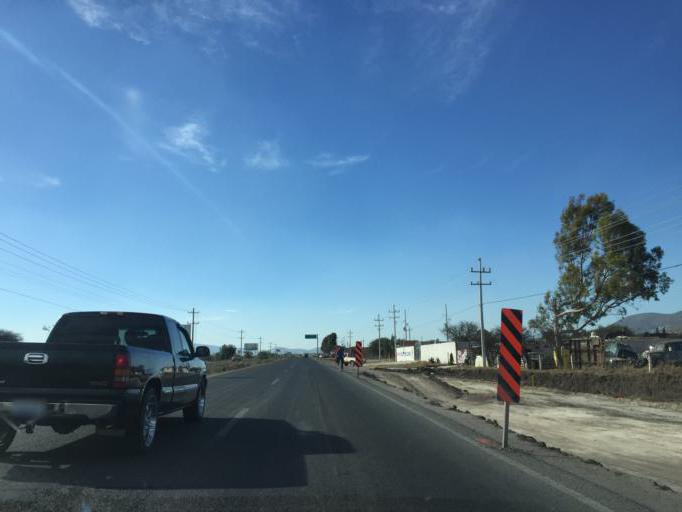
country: MX
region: Queretaro
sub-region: Colon
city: Los Benitos
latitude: 20.6925
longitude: -99.9553
